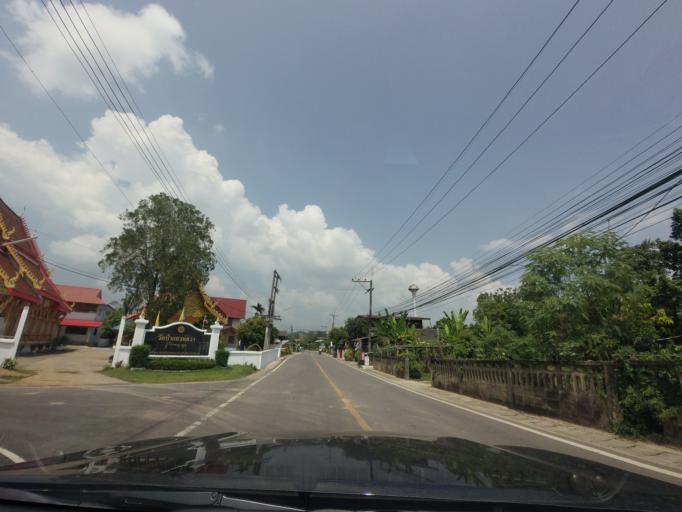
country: TH
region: Nan
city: Santi Suk
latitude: 18.9383
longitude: 100.9261
